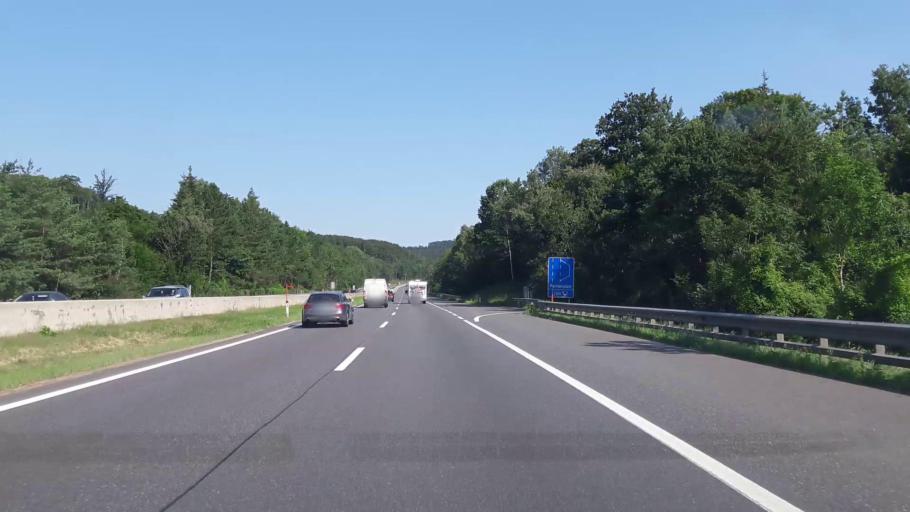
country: AT
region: Lower Austria
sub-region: Politischer Bezirk Baden
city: Klausen-Leopoldsdorf
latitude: 48.1087
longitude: 15.9791
